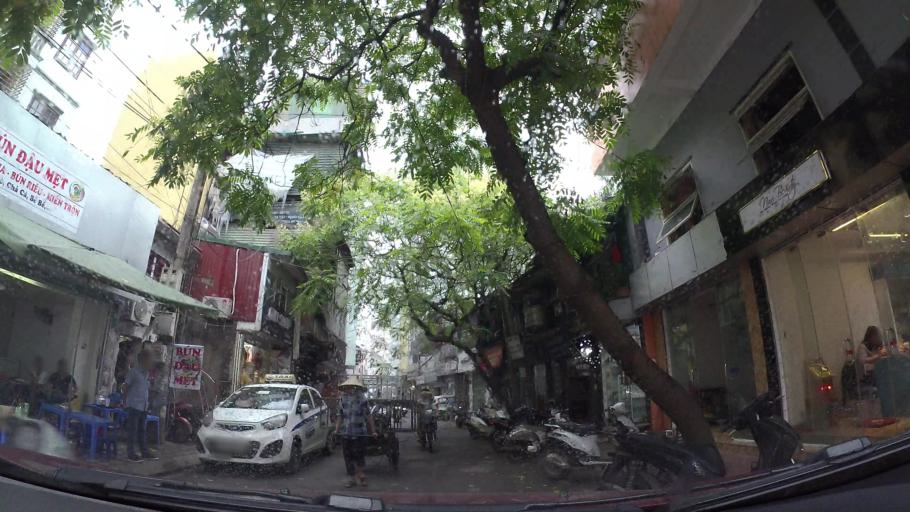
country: VN
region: Ha Noi
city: Dong Da
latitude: 21.0159
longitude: 105.8300
